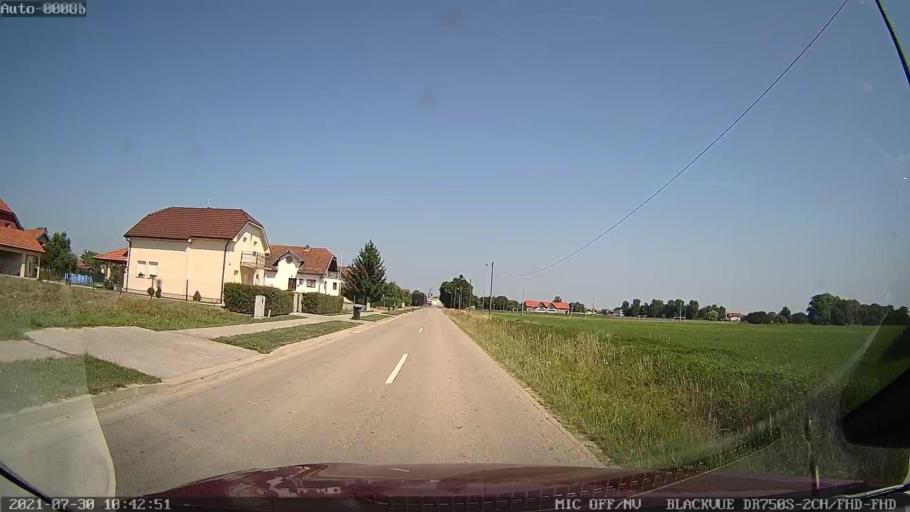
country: HR
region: Medimurska
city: Kursanec
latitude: 46.2886
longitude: 16.4074
